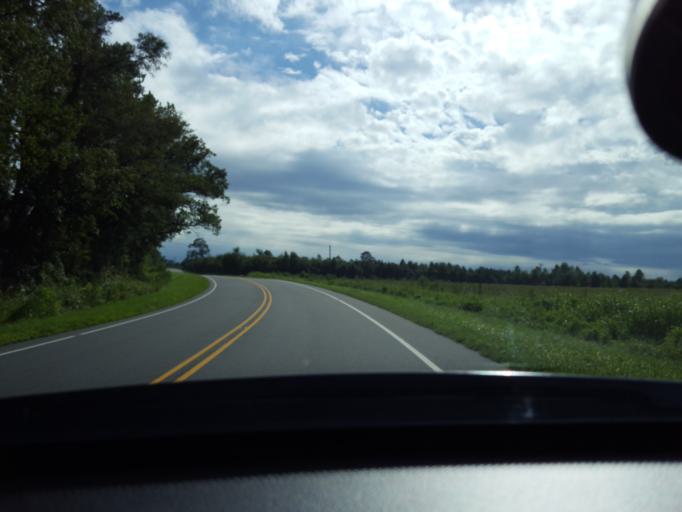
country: US
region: North Carolina
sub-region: Duplin County
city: Kenansville
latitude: 34.9943
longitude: -77.9272
